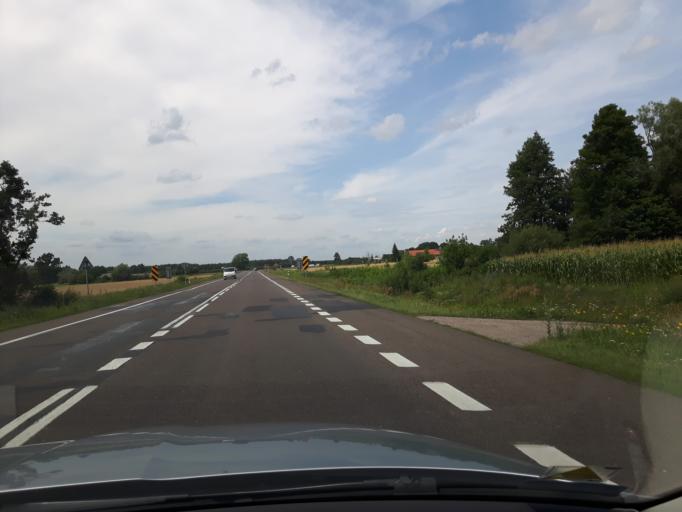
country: PL
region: Masovian Voivodeship
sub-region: Powiat ciechanowski
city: Glinojeck
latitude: 52.7890
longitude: 20.2789
